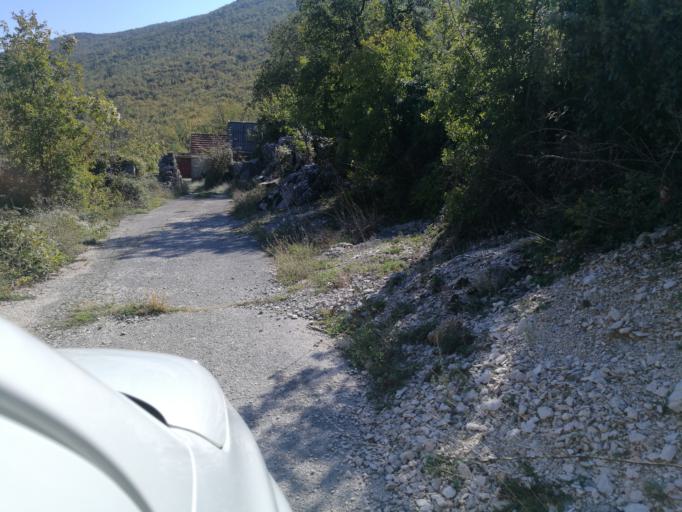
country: HR
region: Splitsko-Dalmatinska
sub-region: Grad Omis
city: Omis
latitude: 43.5130
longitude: 16.7330
